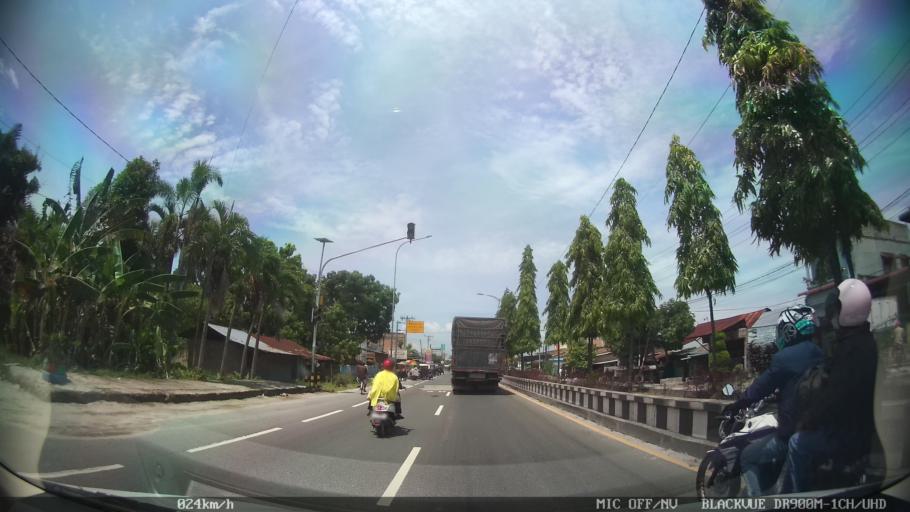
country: ID
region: North Sumatra
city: Perbaungan
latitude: 3.5561
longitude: 98.8853
